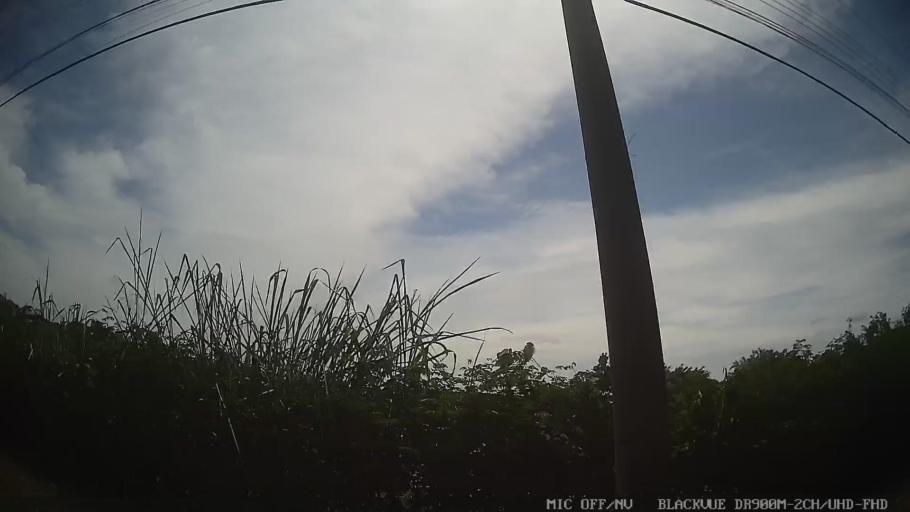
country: BR
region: Sao Paulo
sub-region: Santa Isabel
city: Santa Isabel
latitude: -23.3763
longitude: -46.1794
